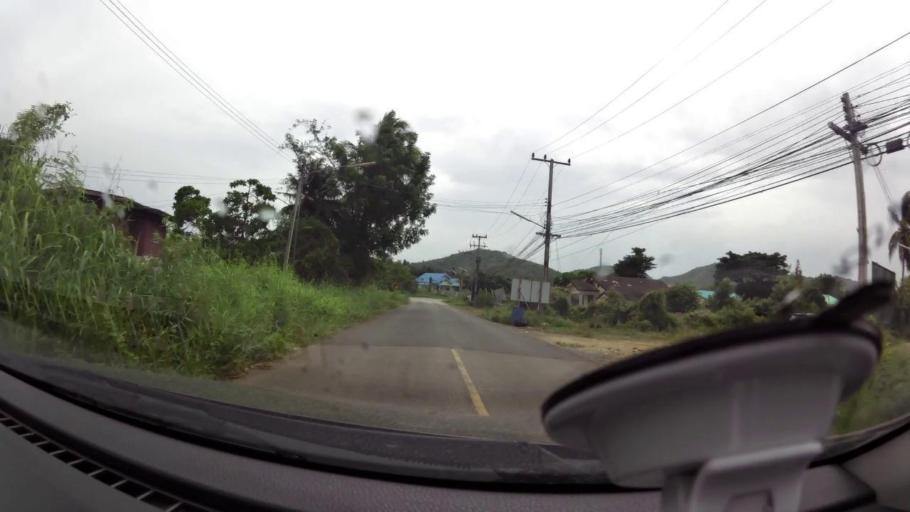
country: TH
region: Prachuap Khiri Khan
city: Pran Buri
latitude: 12.4445
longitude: 99.9684
